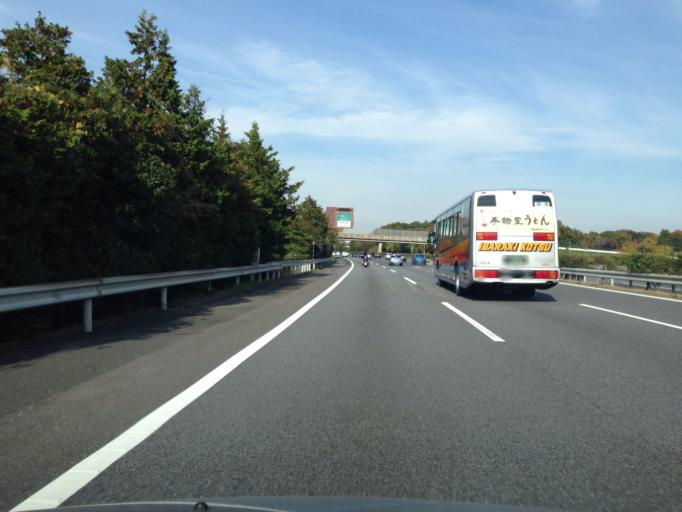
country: JP
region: Ibaraki
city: Naka
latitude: 36.0655
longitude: 140.1577
